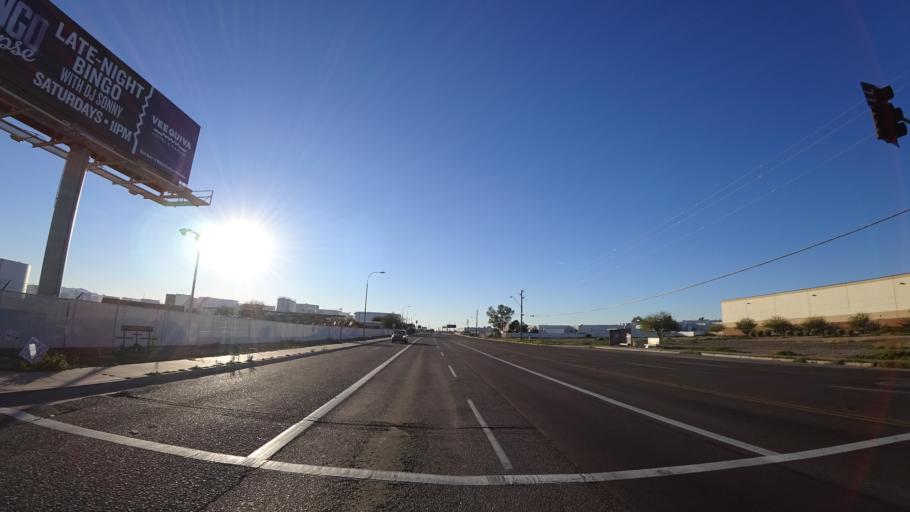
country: US
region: Arizona
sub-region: Maricopa County
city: Laveen
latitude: 33.4512
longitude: -112.1694
